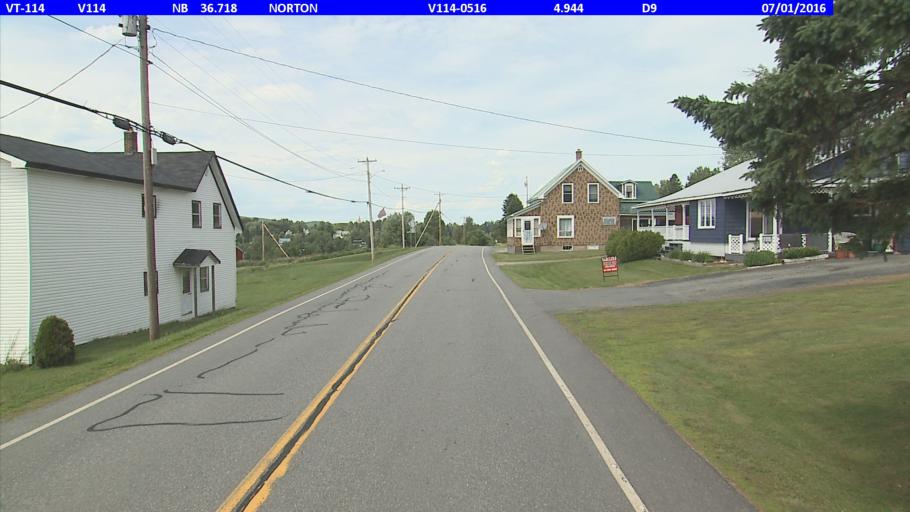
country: CA
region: Quebec
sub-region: Estrie
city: Coaticook
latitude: 45.0037
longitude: -71.7993
